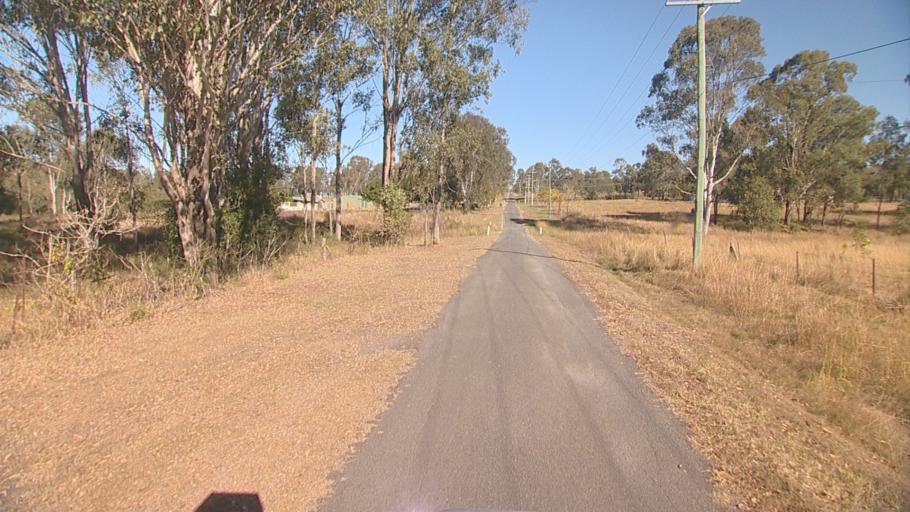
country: AU
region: Queensland
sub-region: Logan
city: North Maclean
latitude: -27.7747
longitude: 153.0252
